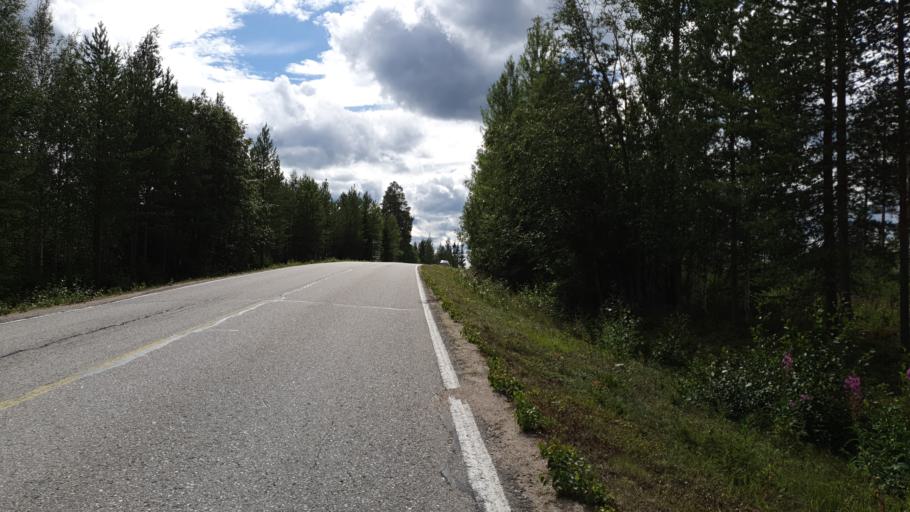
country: FI
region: Kainuu
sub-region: Kehys-Kainuu
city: Kuhmo
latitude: 64.4233
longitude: 29.8155
